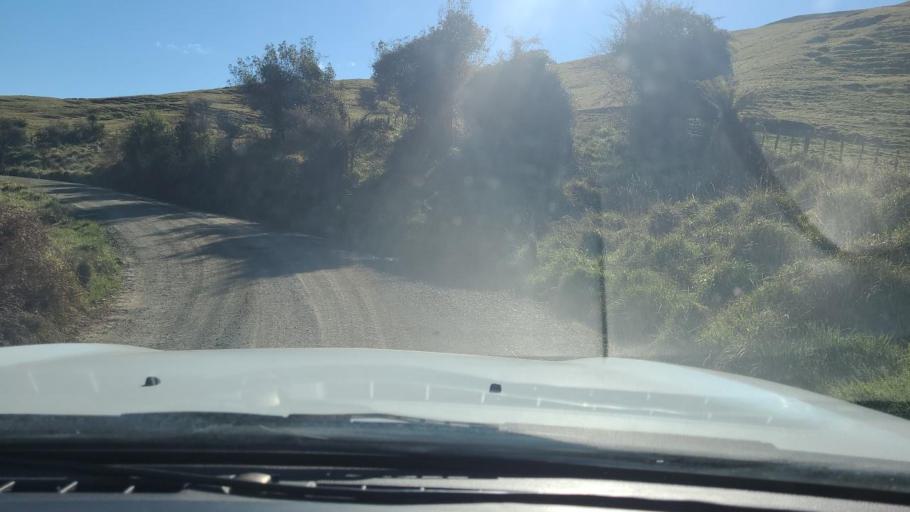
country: NZ
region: Hawke's Bay
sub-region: Napier City
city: Taradale
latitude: -39.2440
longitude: 176.4967
